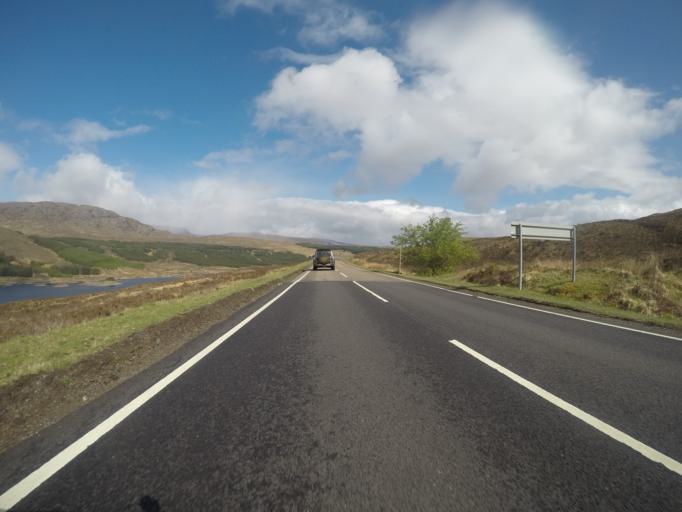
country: GB
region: Scotland
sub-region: Highland
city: Spean Bridge
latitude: 57.1130
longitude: -4.9834
